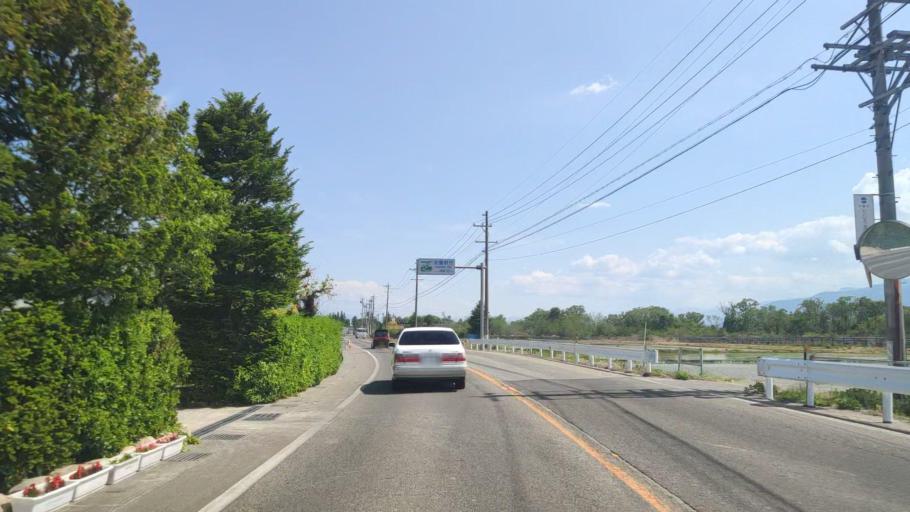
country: JP
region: Nagano
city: Hotaka
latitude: 36.3870
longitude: 137.8651
